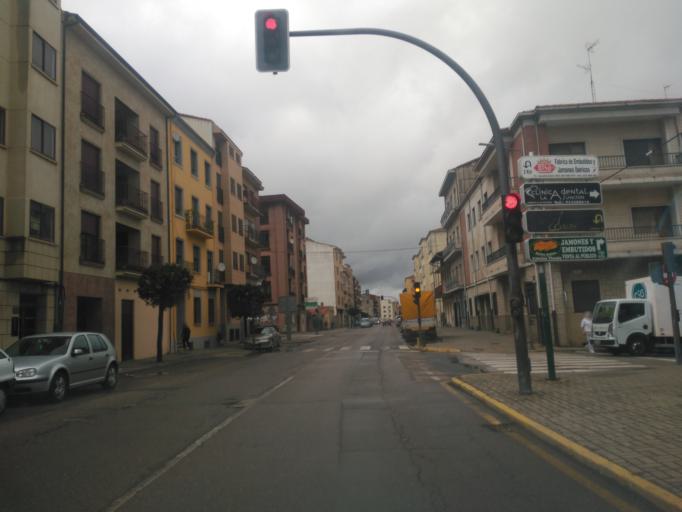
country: ES
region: Castille and Leon
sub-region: Provincia de Salamanca
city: Guijuelo
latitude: 40.5588
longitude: -5.6728
